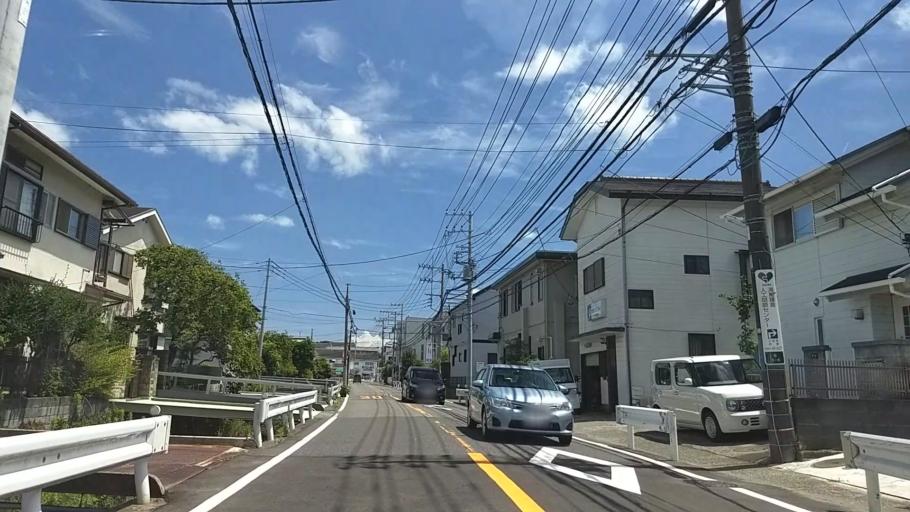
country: JP
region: Kanagawa
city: Kamakura
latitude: 35.3430
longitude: 139.5352
